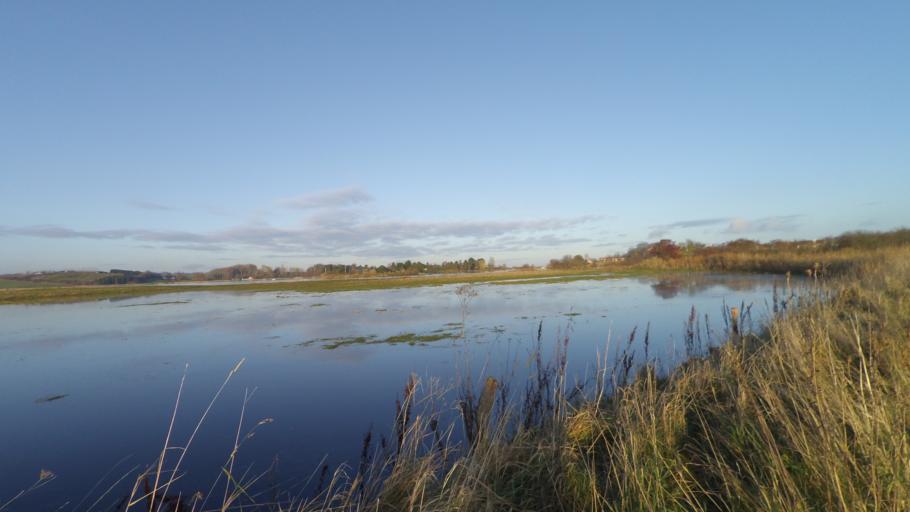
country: DK
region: Central Jutland
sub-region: Arhus Kommune
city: Beder
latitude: 56.0187
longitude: 10.2549
